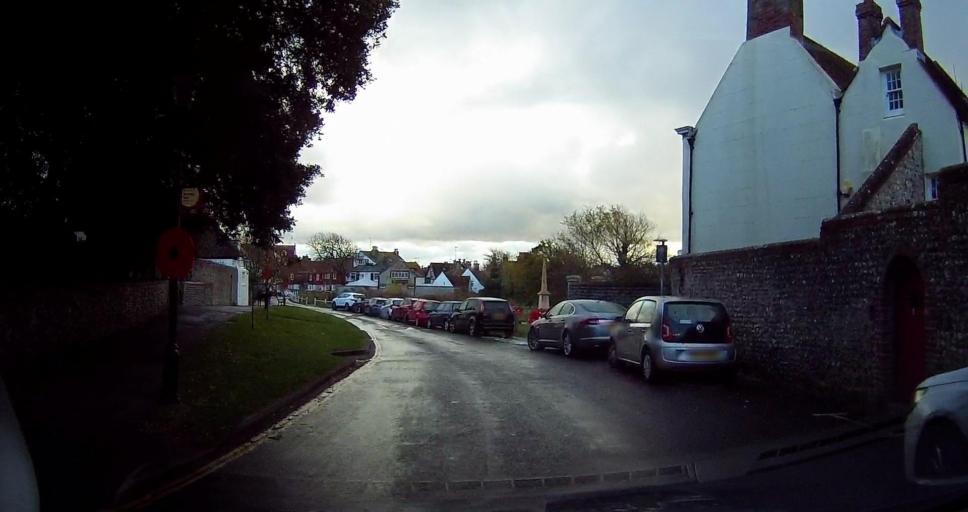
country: GB
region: England
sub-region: Brighton and Hove
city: Rottingdean
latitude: 50.8069
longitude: -0.0582
